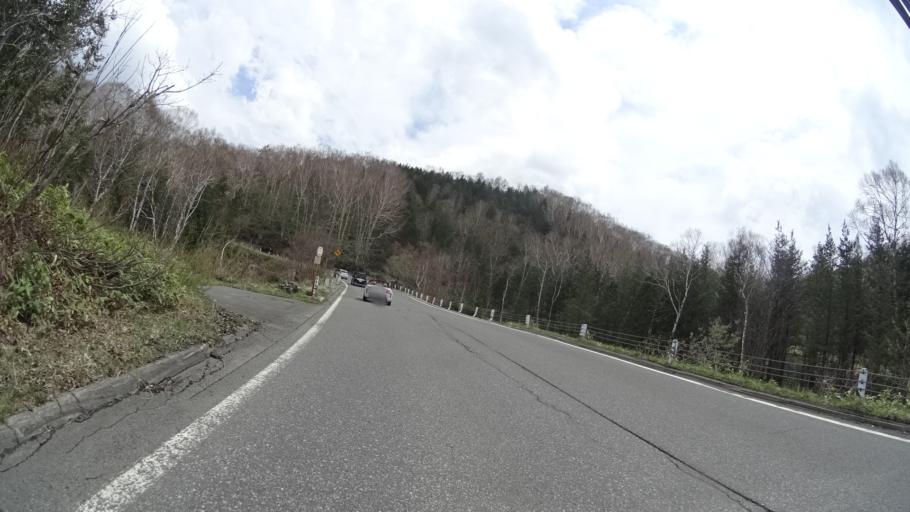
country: JP
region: Nagano
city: Nakano
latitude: 36.7147
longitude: 138.4939
